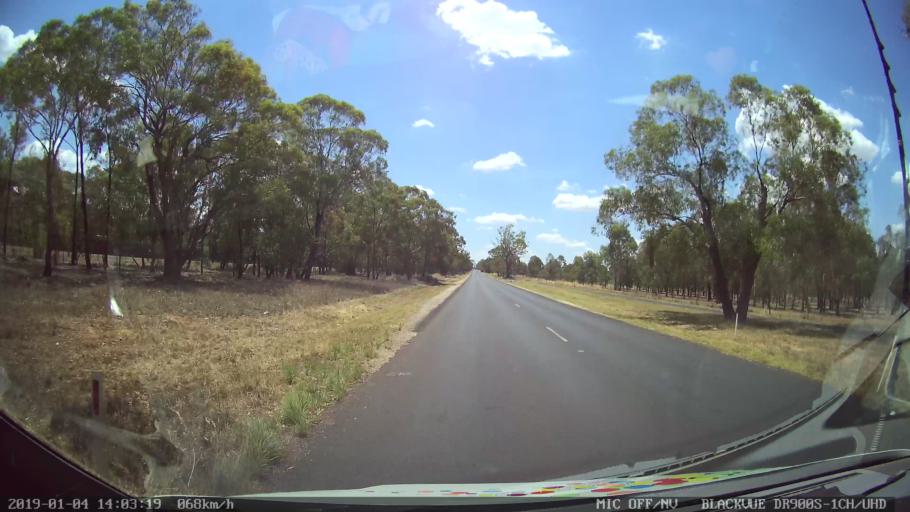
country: AU
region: New South Wales
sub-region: Dubbo Municipality
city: Dubbo
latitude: -32.2786
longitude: 148.5922
